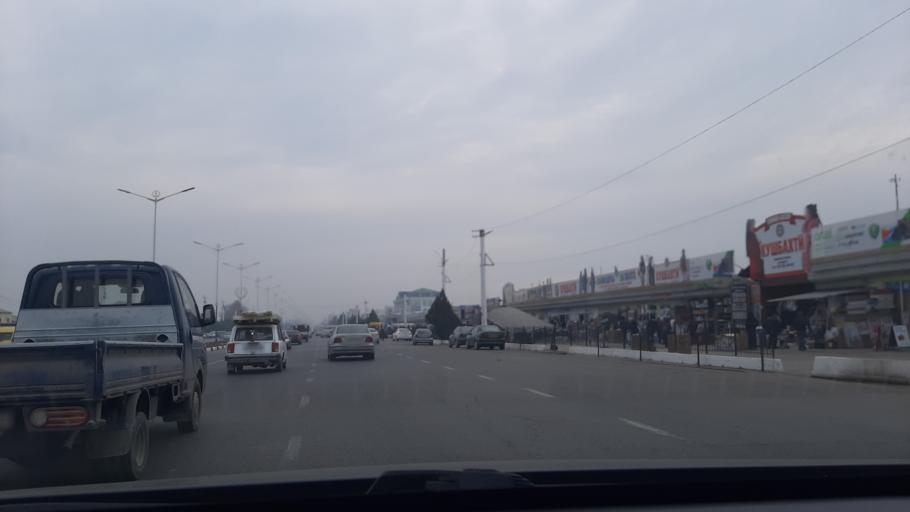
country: TJ
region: Viloyati Sughd
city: Chkalov
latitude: 40.2445
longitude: 69.6998
